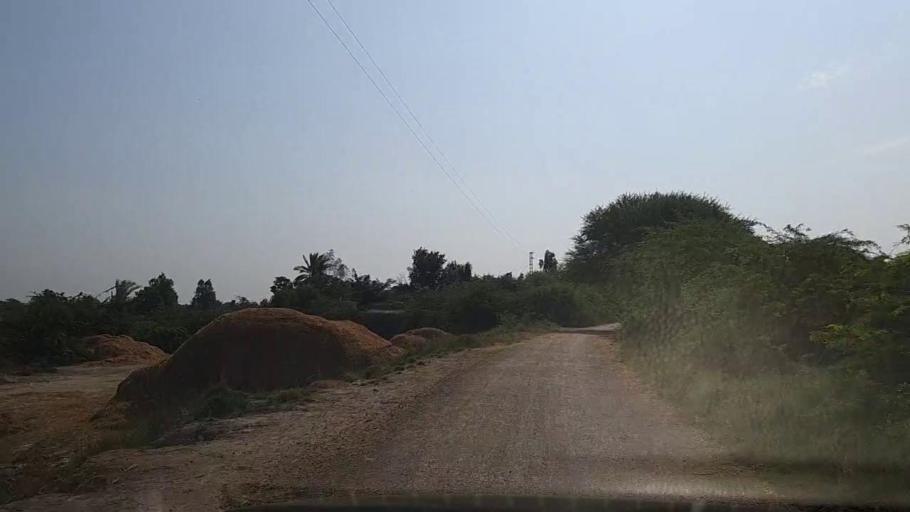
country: PK
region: Sindh
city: Thatta
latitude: 24.7938
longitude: 67.8297
